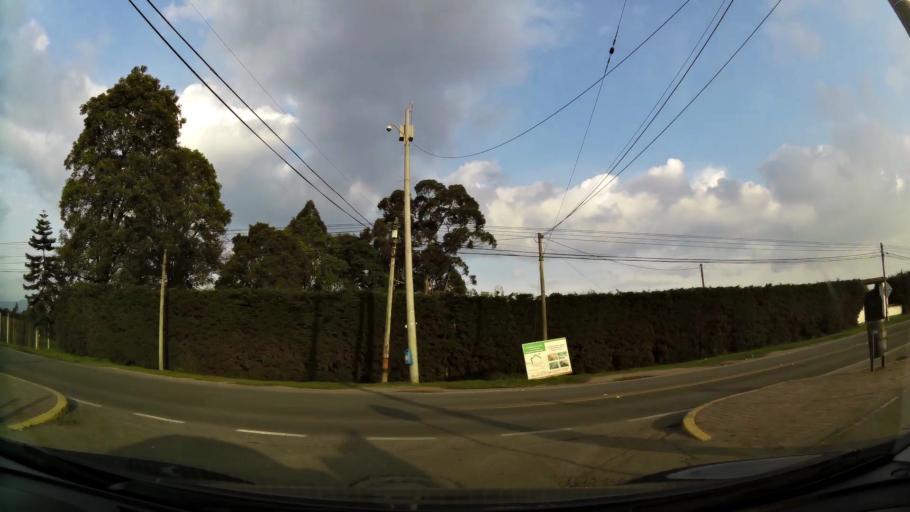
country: CO
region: Cundinamarca
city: Cota
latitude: 4.8203
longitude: -74.0938
